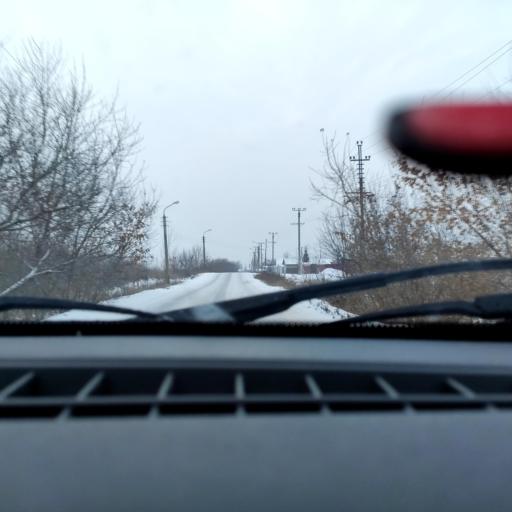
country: RU
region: Bashkortostan
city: Blagoveshchensk
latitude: 54.8898
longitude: 56.0345
